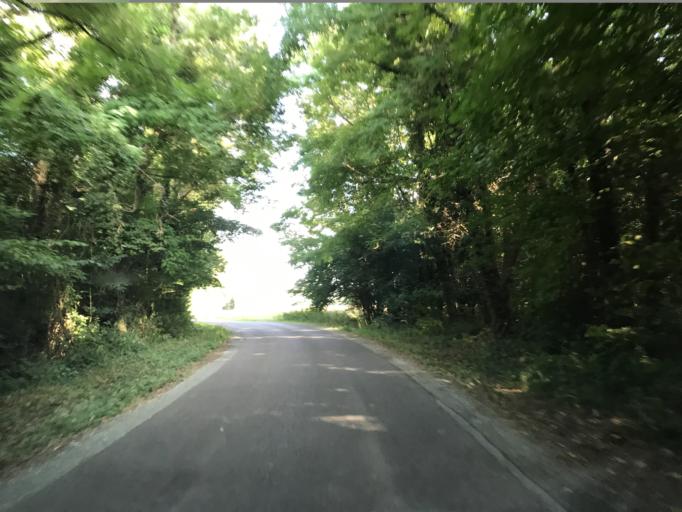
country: FR
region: Haute-Normandie
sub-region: Departement de l'Eure
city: Houlbec-Cocherel
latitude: 49.0567
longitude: 1.3201
